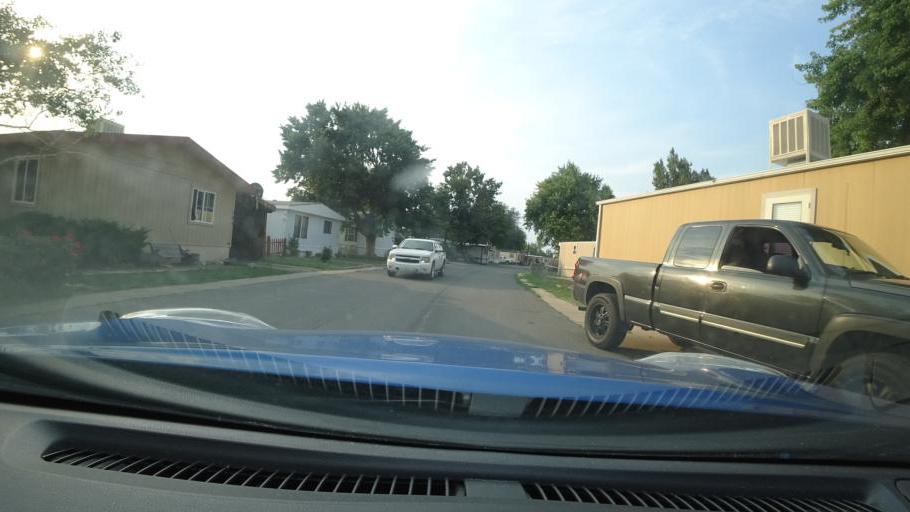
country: US
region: Colorado
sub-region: Adams County
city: Aurora
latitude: 39.7422
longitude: -104.7901
